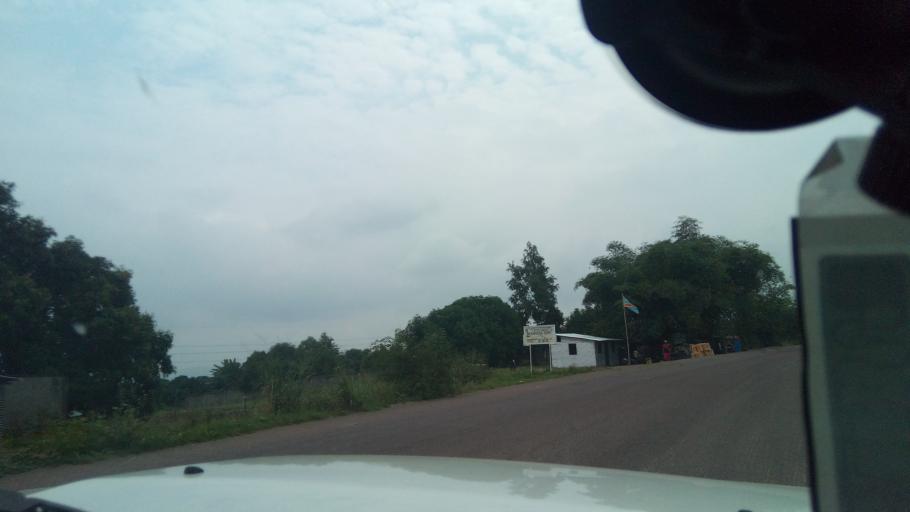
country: CD
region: Kinshasa
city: Masina
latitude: -4.1733
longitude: 15.5429
